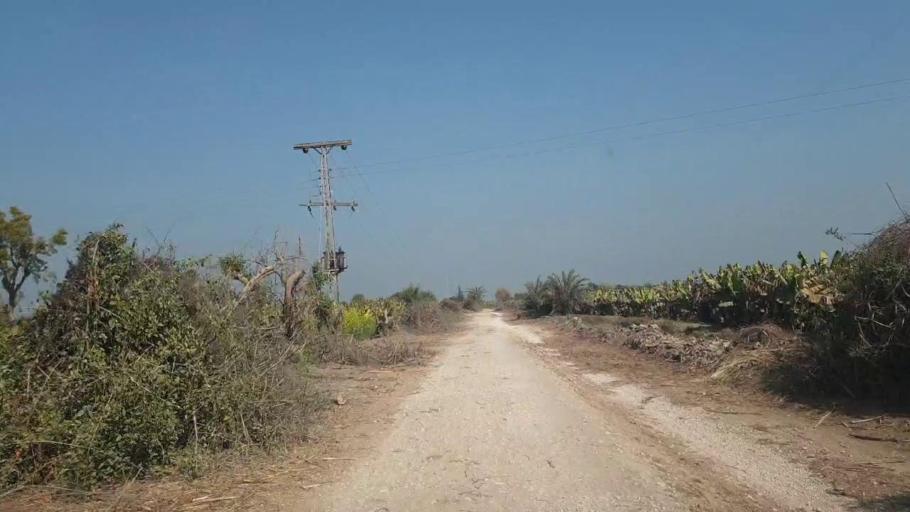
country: PK
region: Sindh
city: Sakrand
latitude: 26.0513
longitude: 68.4477
